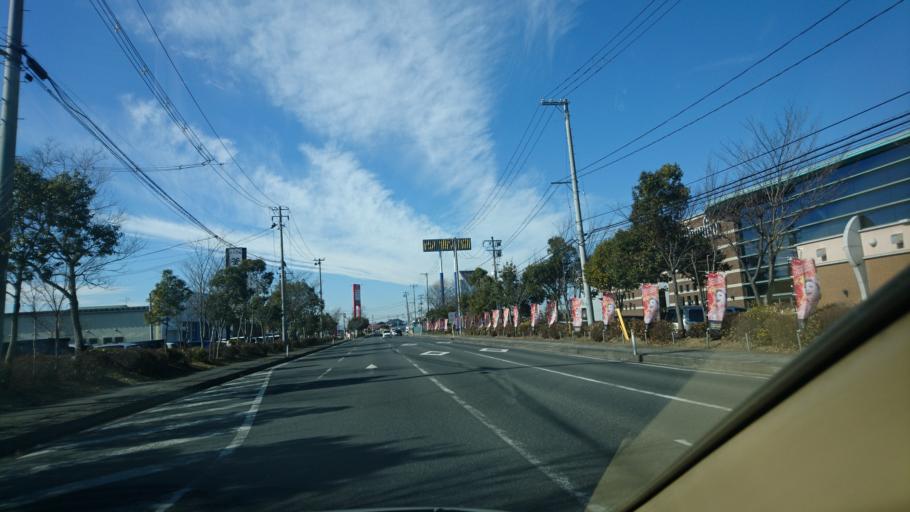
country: JP
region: Miyagi
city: Furukawa
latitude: 38.5992
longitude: 140.9745
